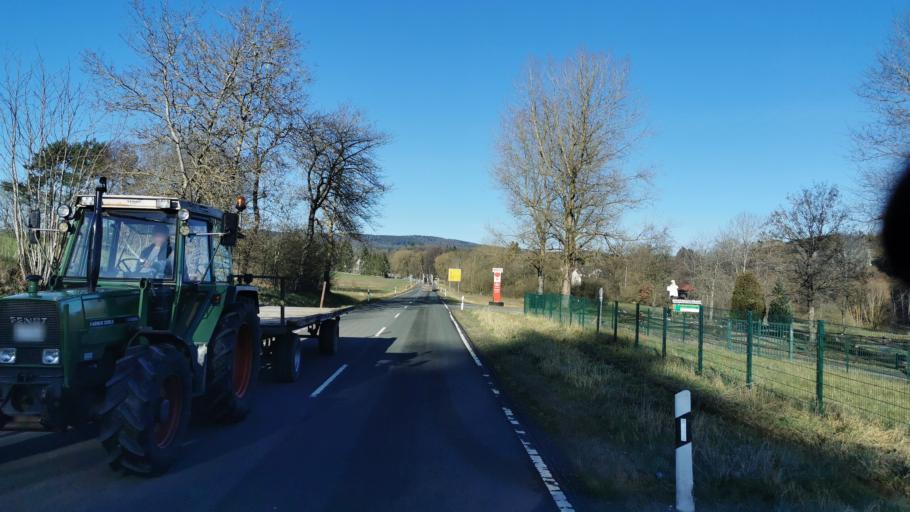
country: DE
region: Rheinland-Pfalz
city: Weidenbach
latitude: 50.1270
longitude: 6.7043
